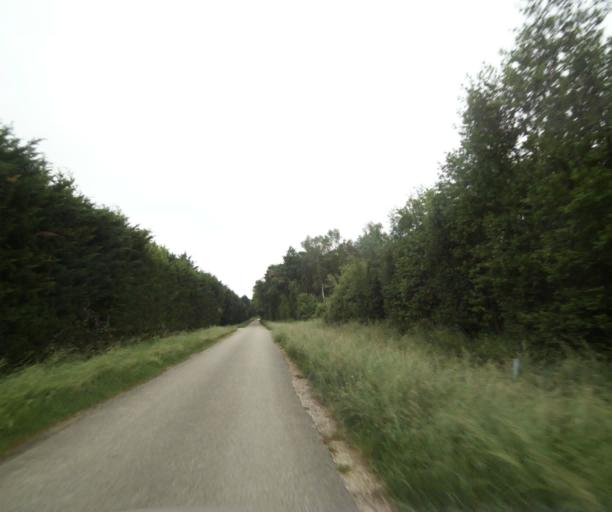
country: FR
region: Rhone-Alpes
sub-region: Departement de l'Ain
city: Mionnay
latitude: 45.8701
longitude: 4.9301
